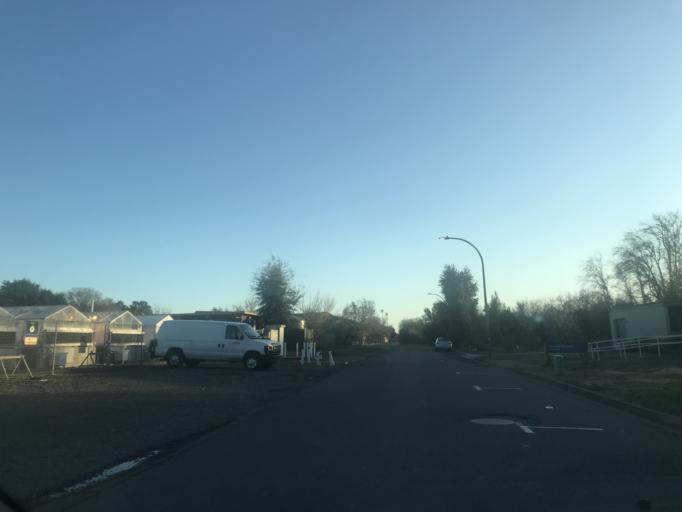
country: US
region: California
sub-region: Yolo County
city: Davis
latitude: 38.5430
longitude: -121.7641
